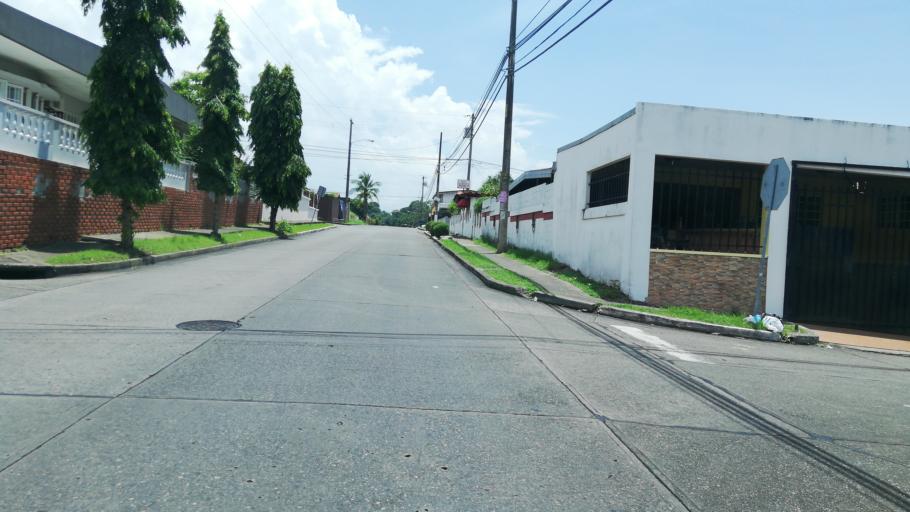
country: PA
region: Panama
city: San Miguelito
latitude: 9.0604
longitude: -79.4570
